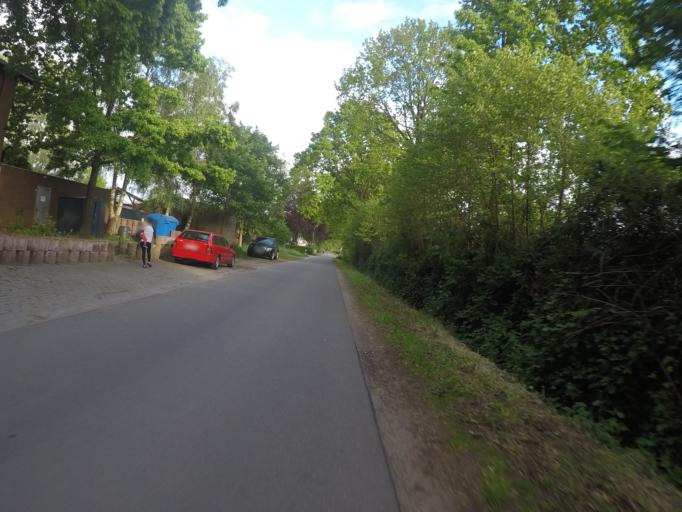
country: DE
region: Schleswig-Holstein
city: Bonningstedt
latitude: 53.6884
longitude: 9.9242
